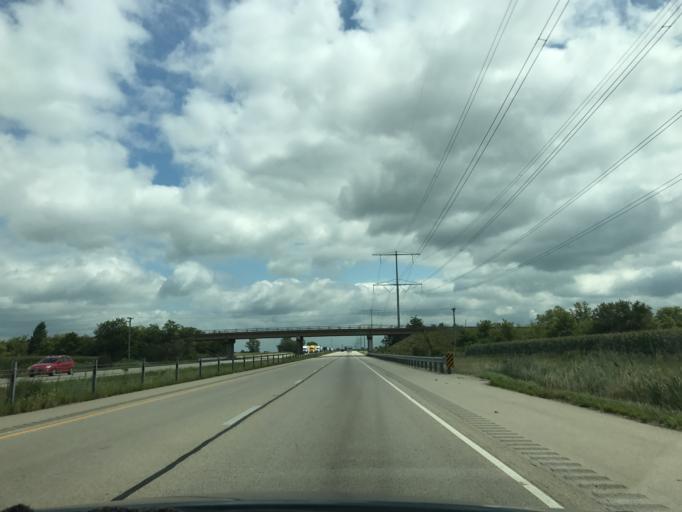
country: US
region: Illinois
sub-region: LaSalle County
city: Seneca
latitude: 41.3768
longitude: -88.5787
